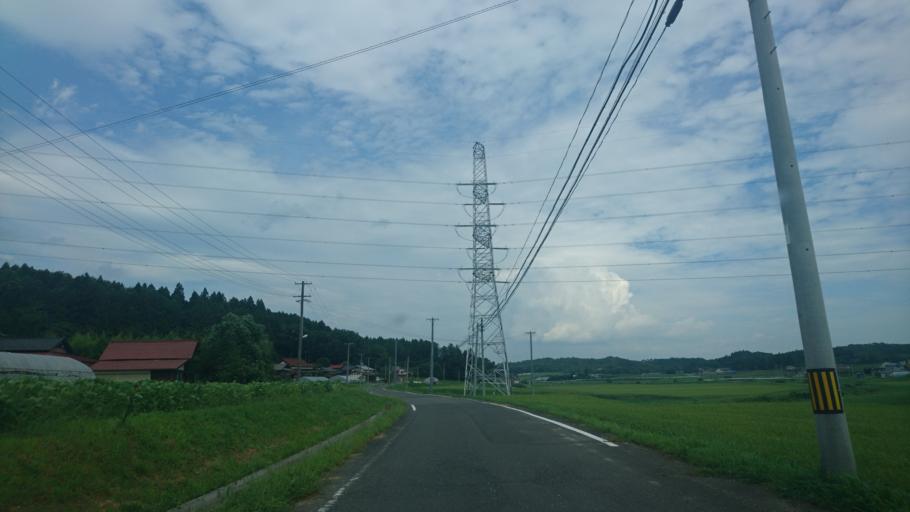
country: JP
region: Miyagi
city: Furukawa
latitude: 38.7638
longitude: 140.9755
